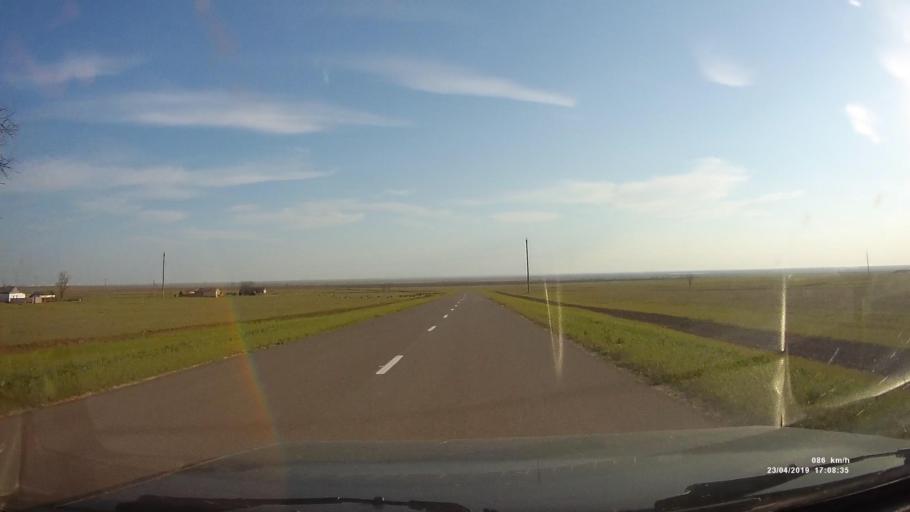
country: RU
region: Kalmykiya
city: Priyutnoye
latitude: 46.2693
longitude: 43.4864
